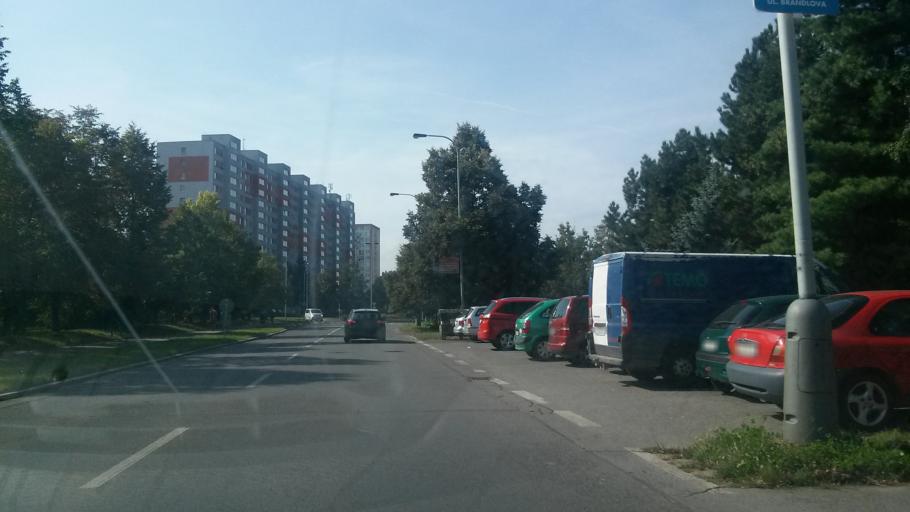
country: CZ
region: Central Bohemia
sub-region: Okres Praha-Zapad
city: Pruhonice
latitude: 50.0329
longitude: 14.5245
